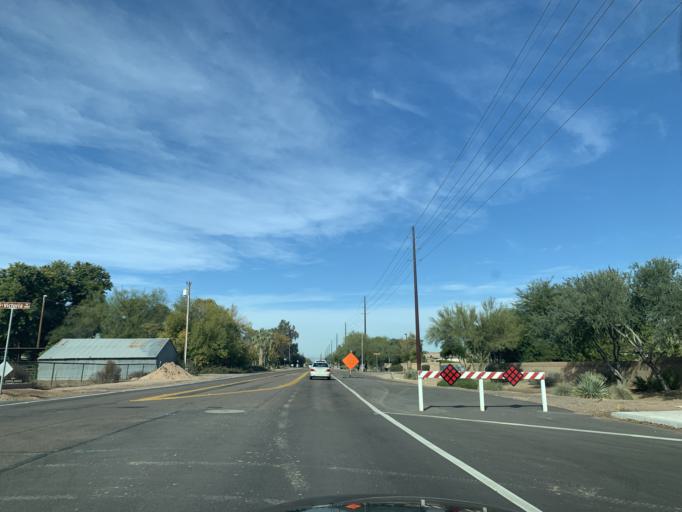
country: US
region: Arizona
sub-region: Maricopa County
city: Sun Lakes
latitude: 33.2226
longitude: -111.8066
